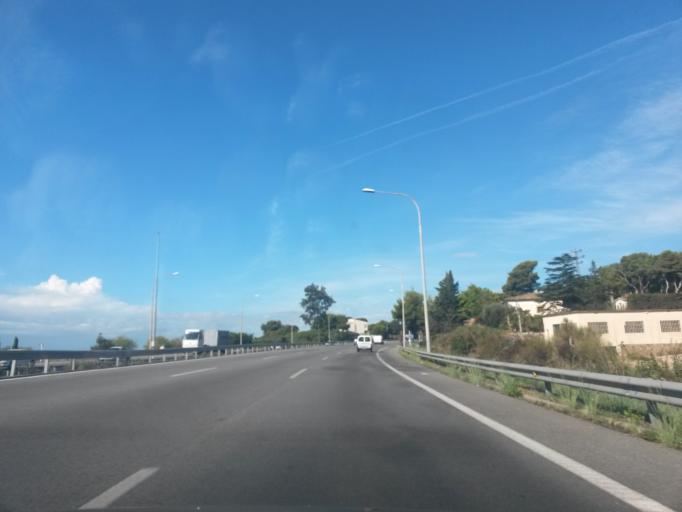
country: ES
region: Catalonia
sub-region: Provincia de Barcelona
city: El Masnou
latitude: 41.4876
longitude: 2.3209
